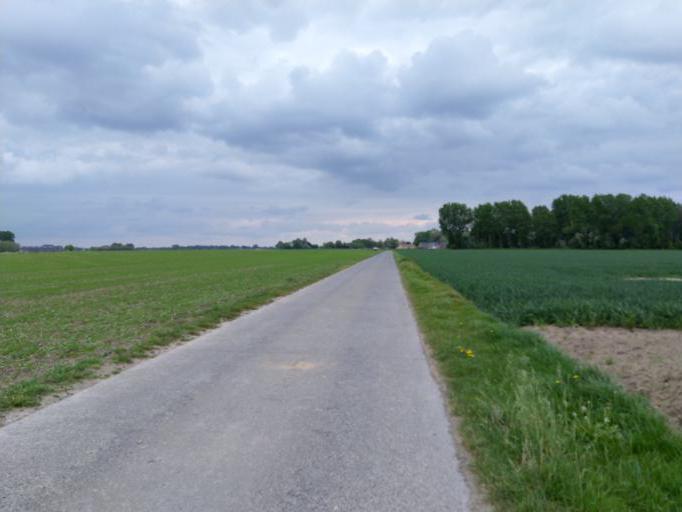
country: BE
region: Wallonia
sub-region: Province du Hainaut
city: Jurbise
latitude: 50.5127
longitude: 3.8817
